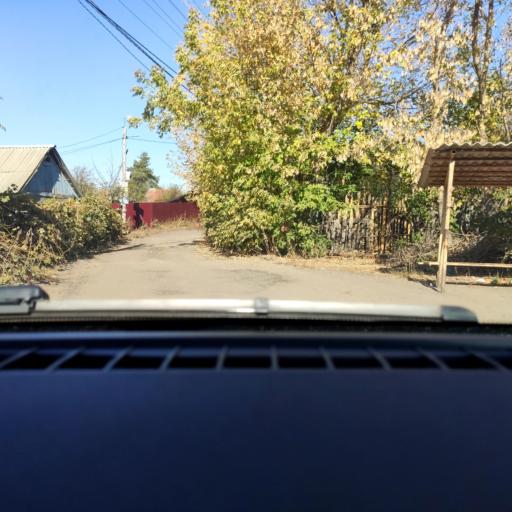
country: RU
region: Voronezj
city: Maslovka
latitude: 51.6032
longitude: 39.2779
